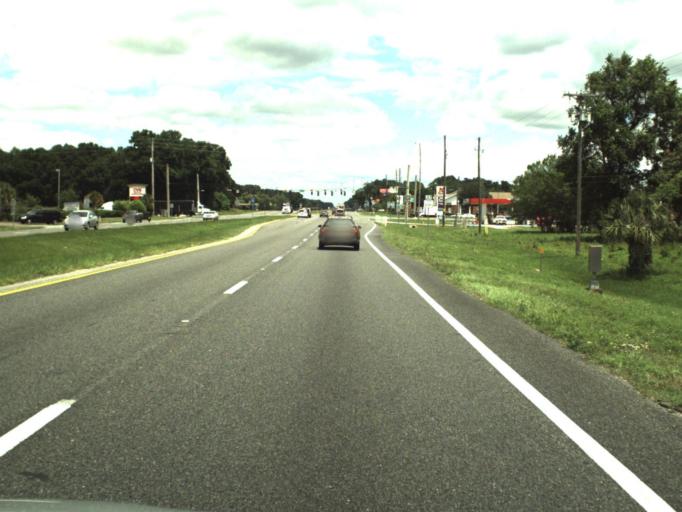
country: US
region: Florida
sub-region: Marion County
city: Ocala
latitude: 29.2573
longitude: -82.1519
